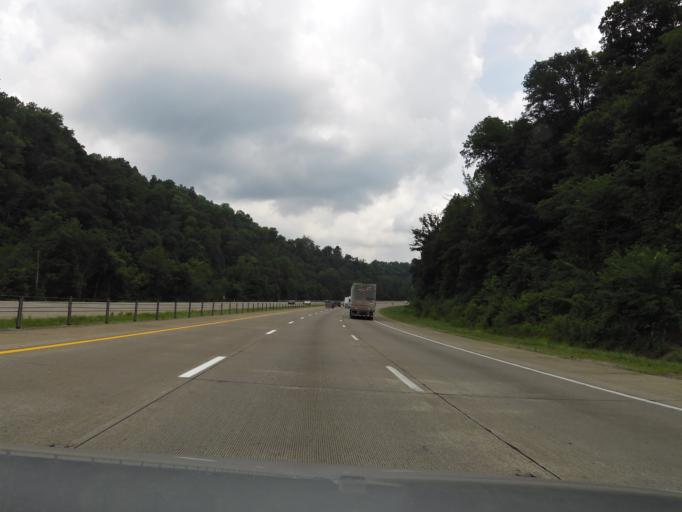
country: US
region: Kentucky
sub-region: Hardin County
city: Elizabethtown
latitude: 37.7553
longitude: -85.7959
